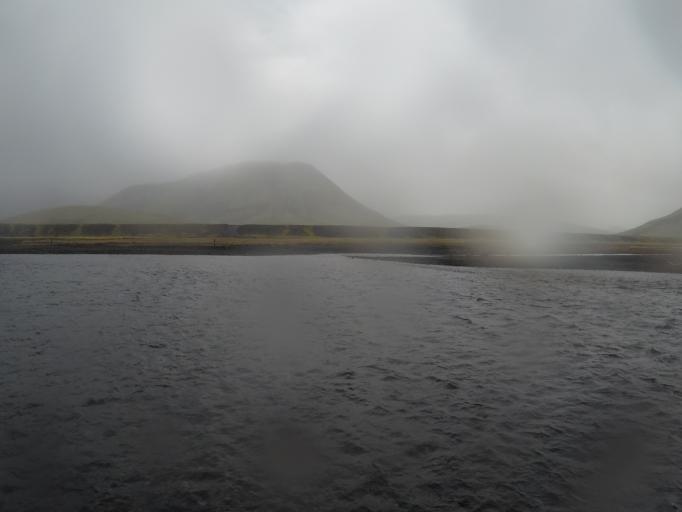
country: IS
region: South
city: Vestmannaeyjar
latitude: 63.9685
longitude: -18.8161
